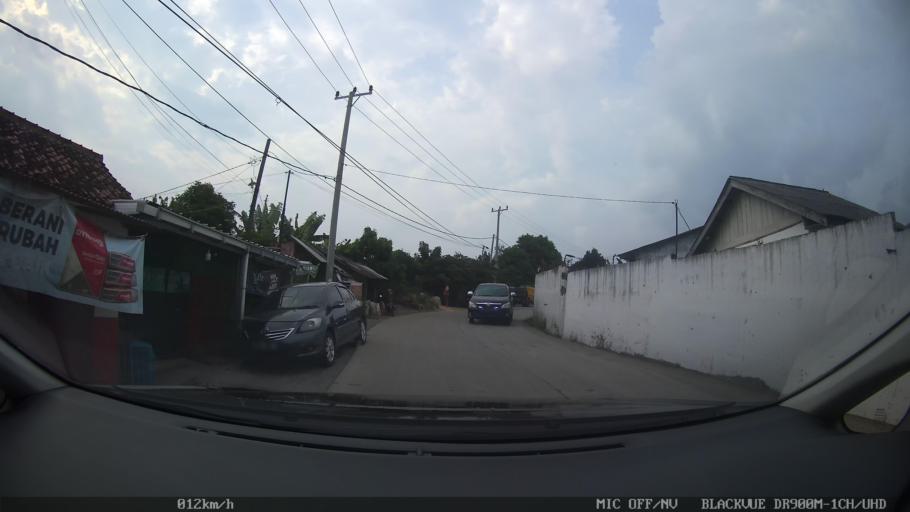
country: ID
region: Lampung
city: Bandarlampung
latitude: -5.4343
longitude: 105.2959
